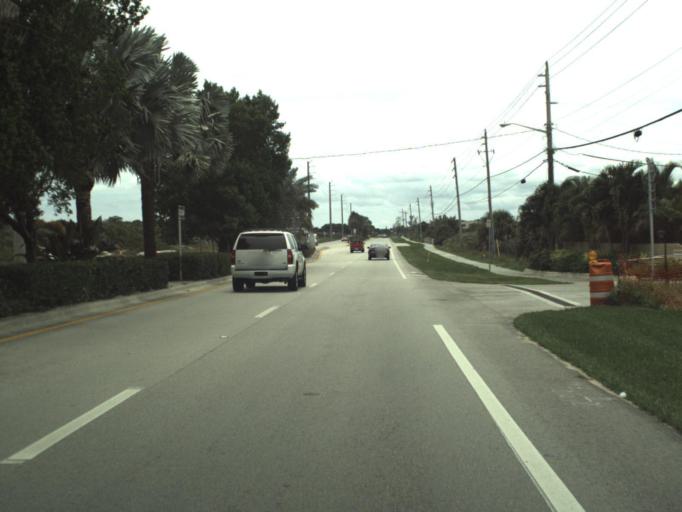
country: US
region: Florida
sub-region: Palm Beach County
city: Juno Beach
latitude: 26.8916
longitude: -80.0595
